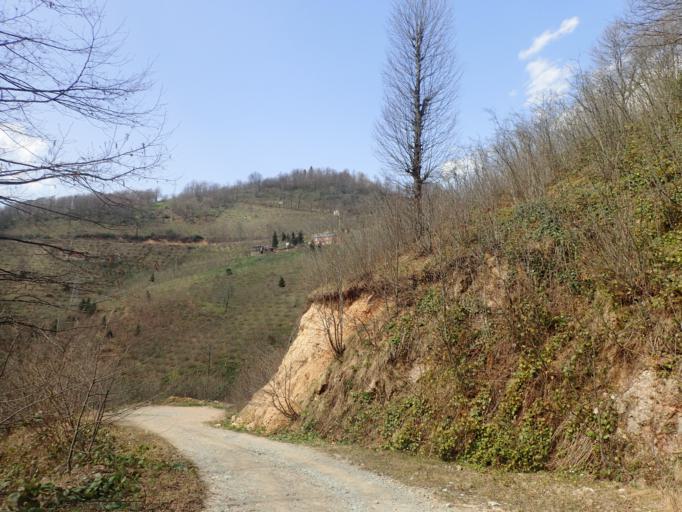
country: TR
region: Ordu
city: Kabaduz
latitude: 40.8182
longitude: 37.9041
